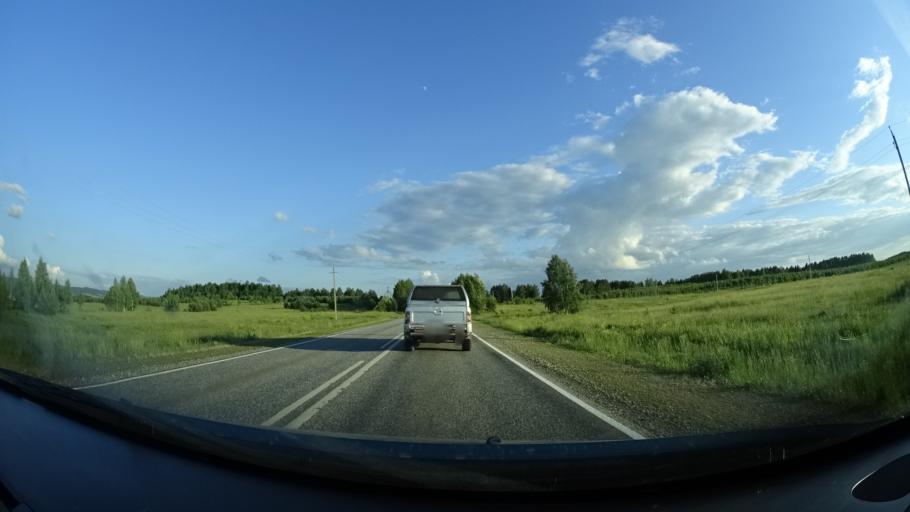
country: RU
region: Perm
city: Osa
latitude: 57.1661
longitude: 55.5311
